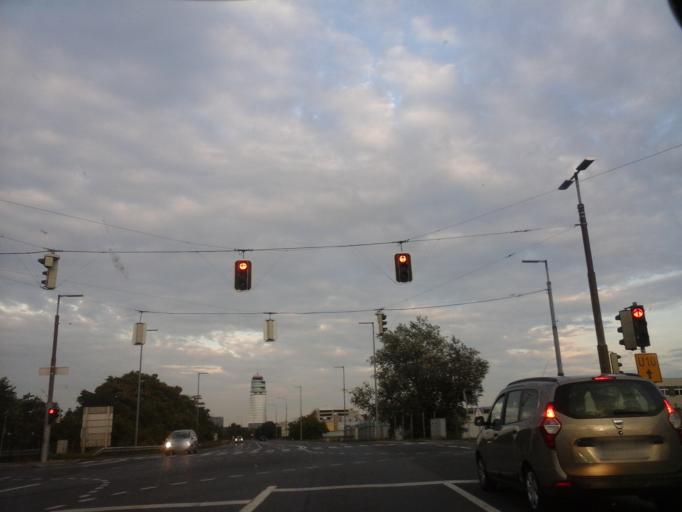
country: AT
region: Lower Austria
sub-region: Politischer Bezirk Wien-Umgebung
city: Rauchenwarth
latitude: 48.1270
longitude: 16.5487
